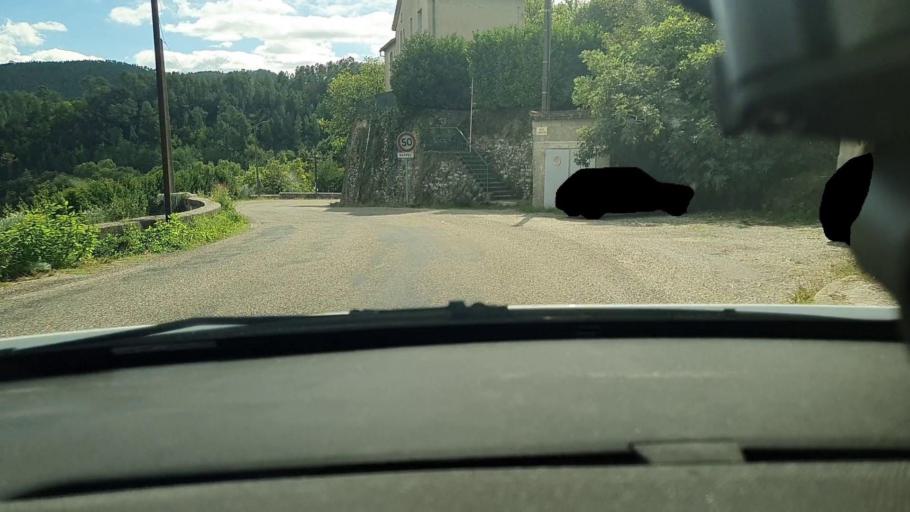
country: FR
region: Languedoc-Roussillon
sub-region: Departement du Gard
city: Besseges
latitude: 44.3003
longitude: 4.0617
